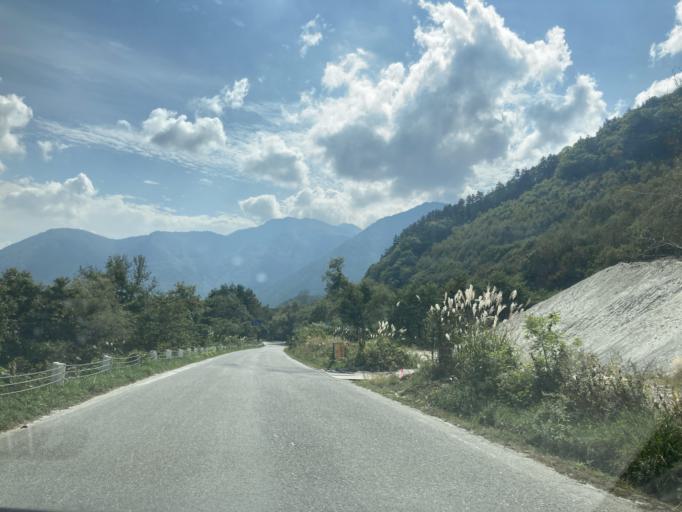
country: JP
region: Nagano
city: Omachi
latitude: 36.5281
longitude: 137.7903
